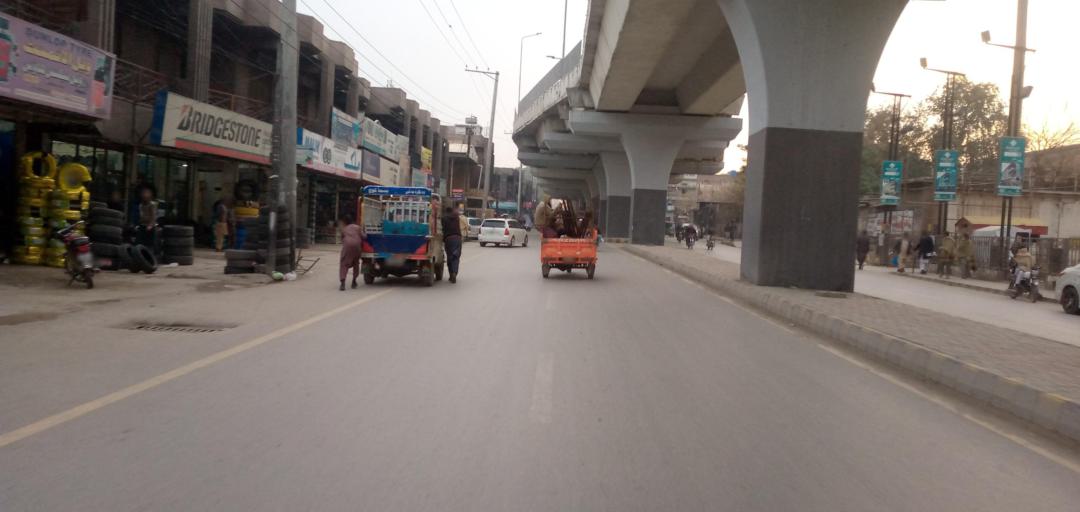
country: PK
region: Khyber Pakhtunkhwa
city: Peshawar
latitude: 33.9998
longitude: 71.5456
